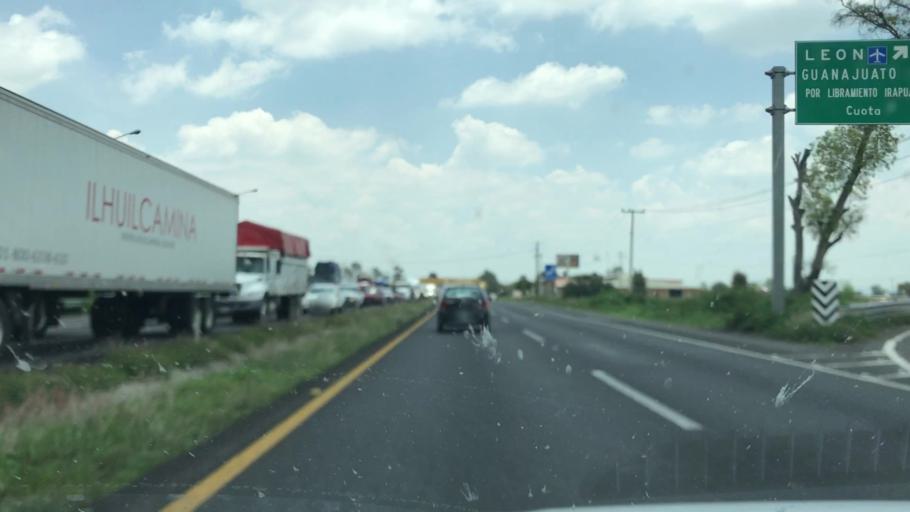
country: MX
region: Guanajuato
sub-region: Irapuato
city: Colonia Morelos de Guadalupe de Rivera
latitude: 20.5946
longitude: -101.4222
